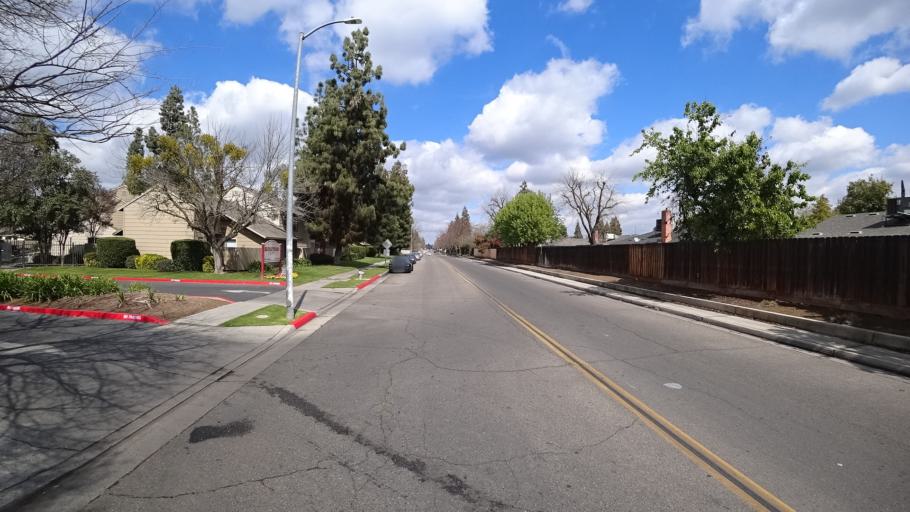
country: US
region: California
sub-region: Fresno County
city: West Park
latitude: 36.8231
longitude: -119.8626
